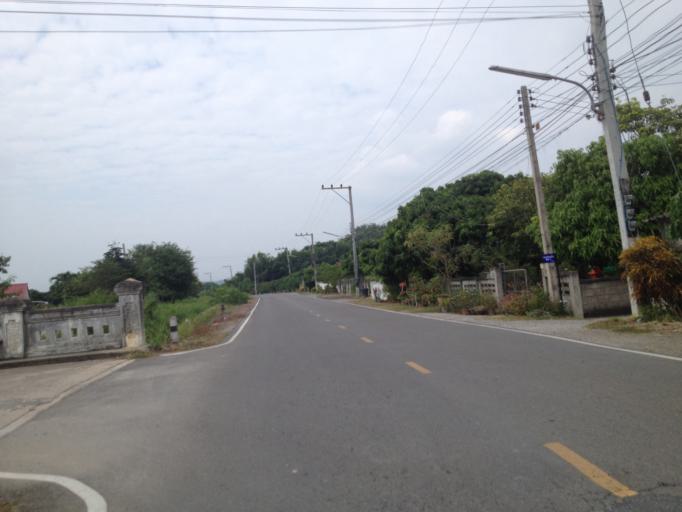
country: TH
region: Chiang Mai
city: San Pa Tong
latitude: 18.6566
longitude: 98.8848
